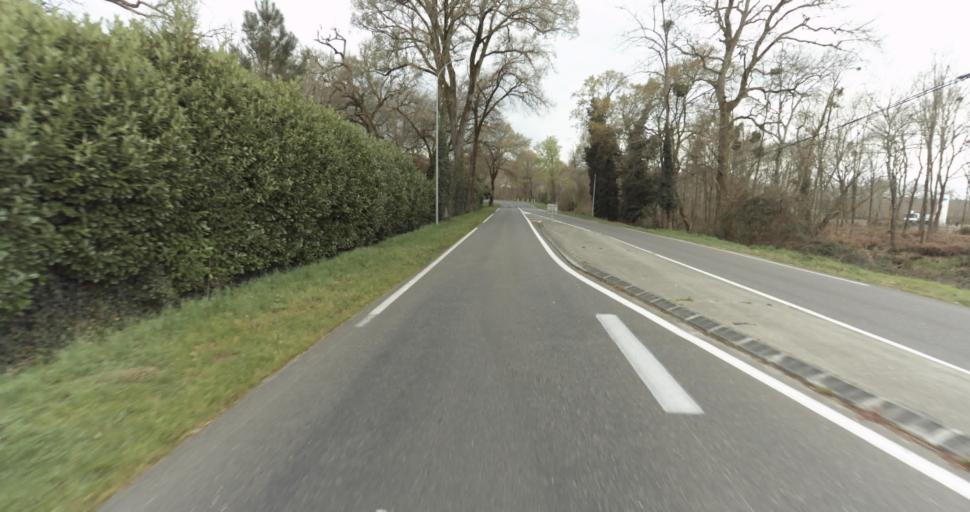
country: FR
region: Aquitaine
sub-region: Departement des Landes
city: Roquefort
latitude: 44.0220
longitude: -0.3400
